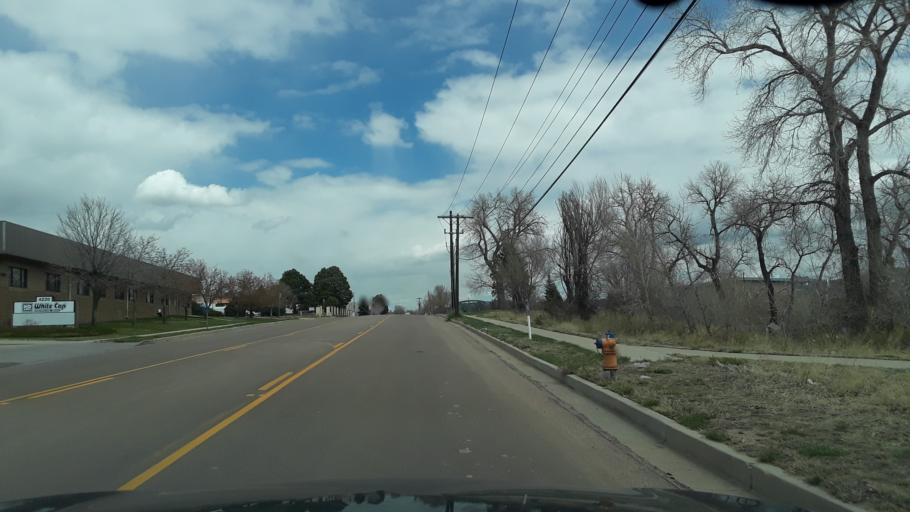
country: US
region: Colorado
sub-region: El Paso County
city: Colorado Springs
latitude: 38.8917
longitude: -104.8256
